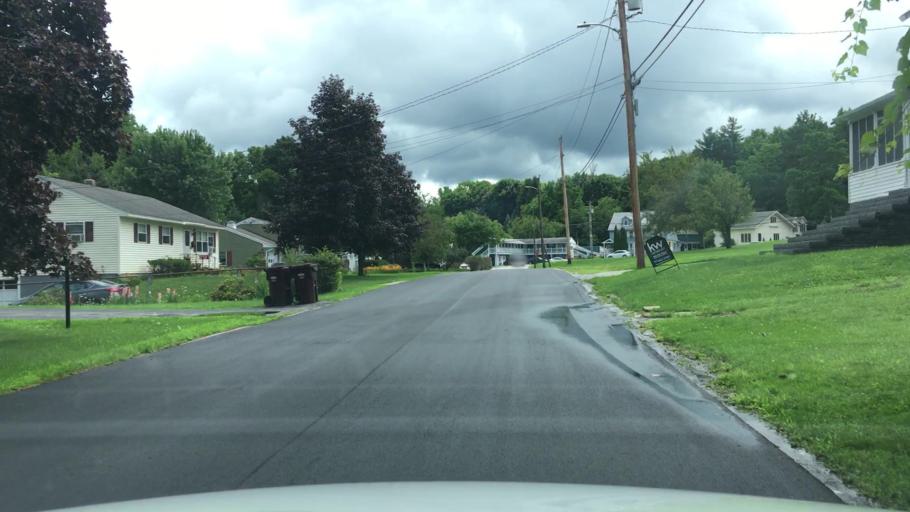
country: US
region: Vermont
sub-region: Bennington County
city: Bennington
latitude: 42.8838
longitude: -73.2070
